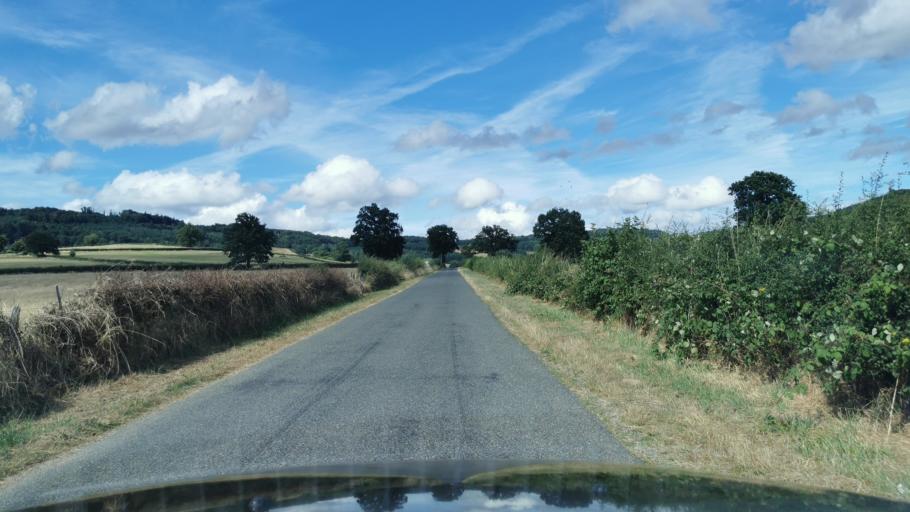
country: FR
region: Bourgogne
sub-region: Departement de Saone-et-Loire
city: Marmagne
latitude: 46.8600
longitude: 4.3076
